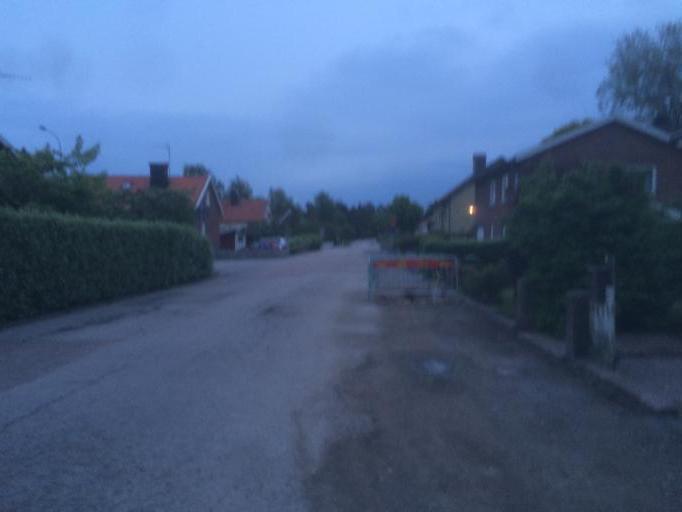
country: SE
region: Vaestra Goetaland
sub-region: Vanersborgs Kommun
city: Vanersborg
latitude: 58.3616
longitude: 12.3491
